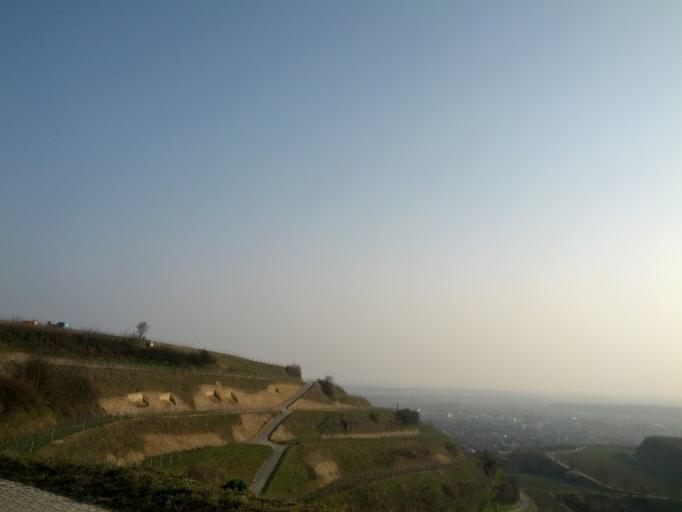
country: DE
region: Baden-Wuerttemberg
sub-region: Freiburg Region
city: Ihringen
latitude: 48.0543
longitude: 7.6466
